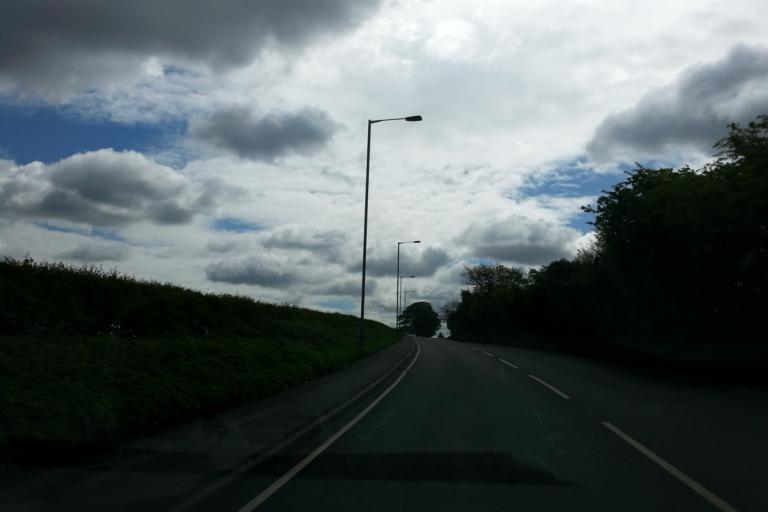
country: GB
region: England
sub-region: Staffordshire
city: Essington
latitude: 52.6566
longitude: -2.0594
